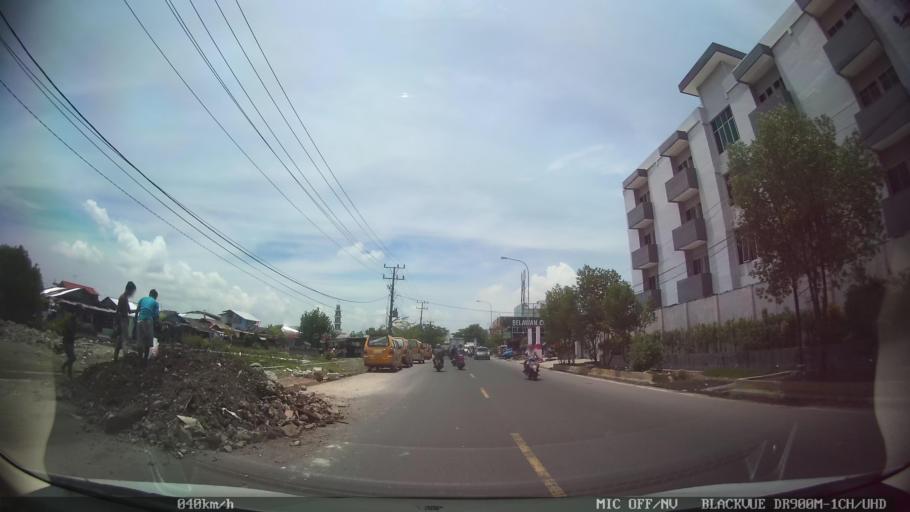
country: ID
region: North Sumatra
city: Belawan
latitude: 3.7742
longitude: 98.6813
